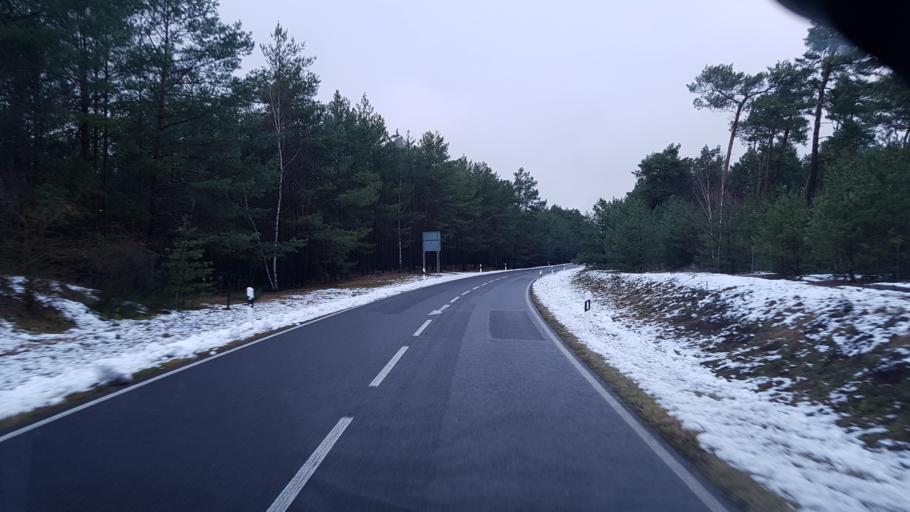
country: DE
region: Brandenburg
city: Janschwalde
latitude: 51.8493
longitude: 14.5071
